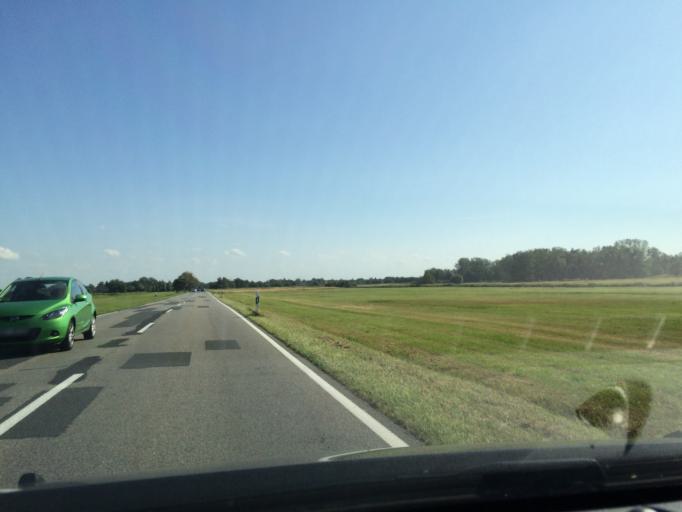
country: DE
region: Mecklenburg-Vorpommern
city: Zingst
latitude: 54.3907
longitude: 12.6775
